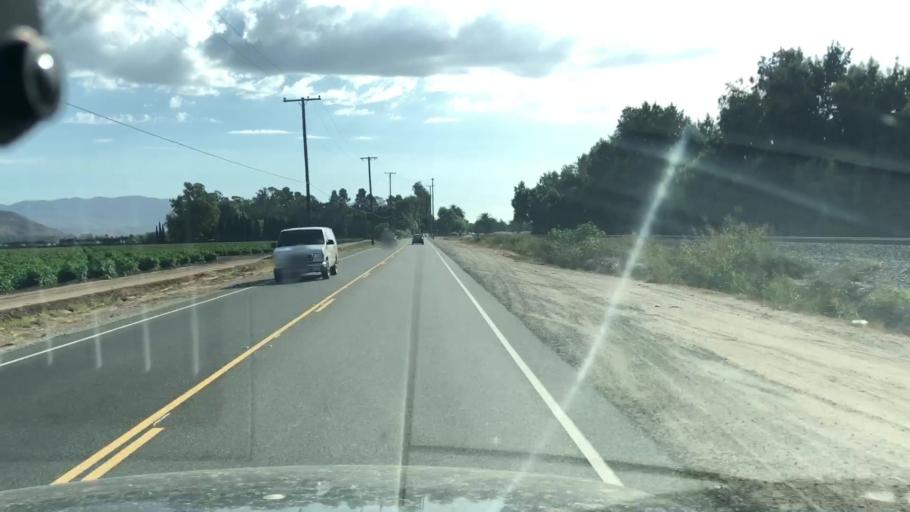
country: US
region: California
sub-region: Ventura County
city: Camarillo
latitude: 34.2027
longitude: -119.0423
